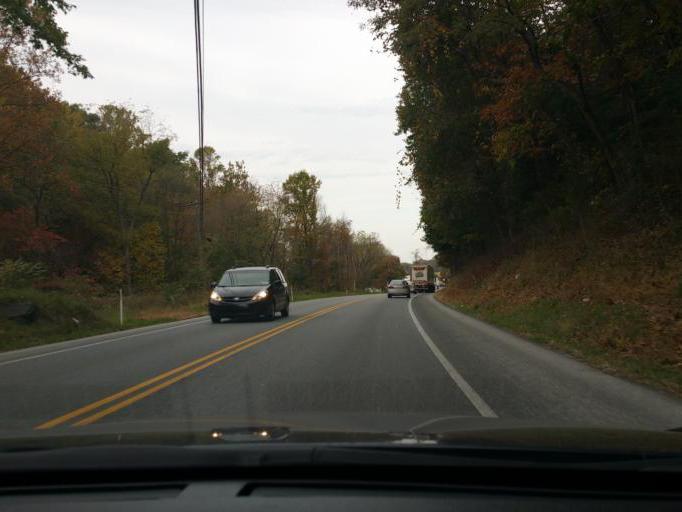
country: US
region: Pennsylvania
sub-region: Lancaster County
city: Quarryville
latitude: 39.9124
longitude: -76.1872
